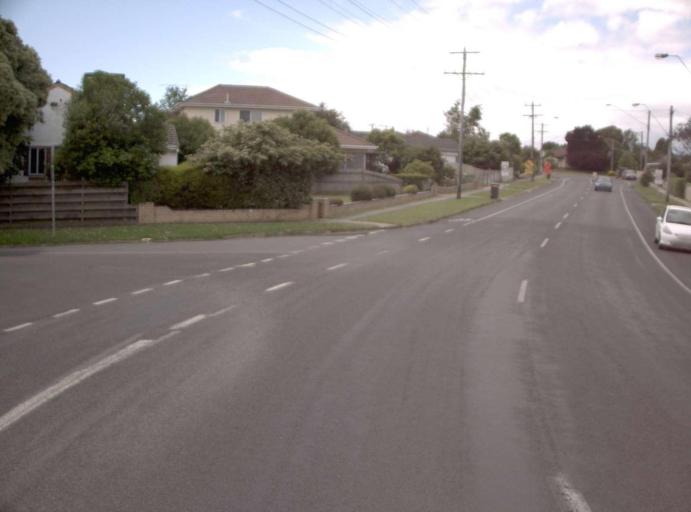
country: AU
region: Victoria
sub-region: Baw Baw
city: Warragul
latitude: -38.1494
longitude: 145.9360
